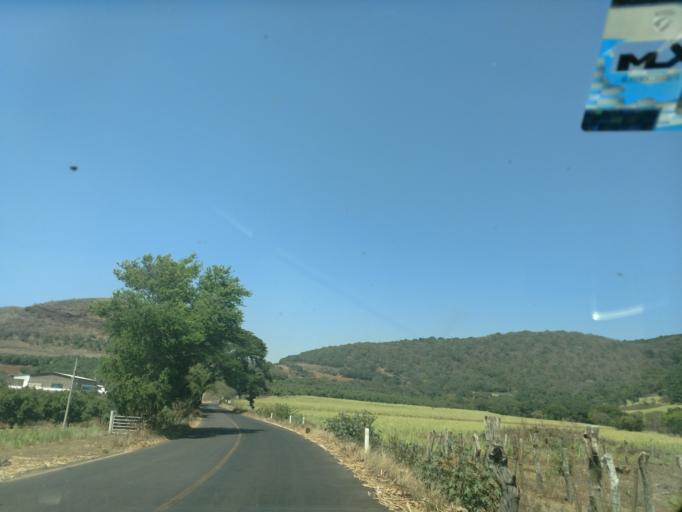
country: MX
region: Nayarit
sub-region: Tepic
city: La Corregidora
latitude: 21.4982
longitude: -104.7800
